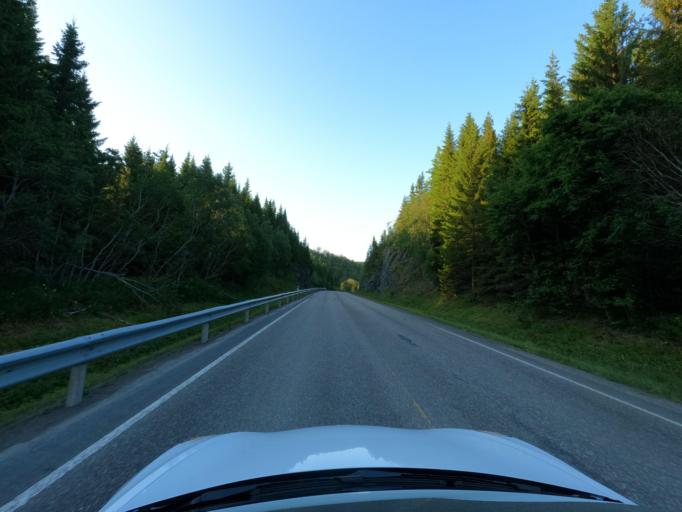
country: NO
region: Troms
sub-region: Harstad
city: Harstad
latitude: 68.7178
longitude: 16.5090
